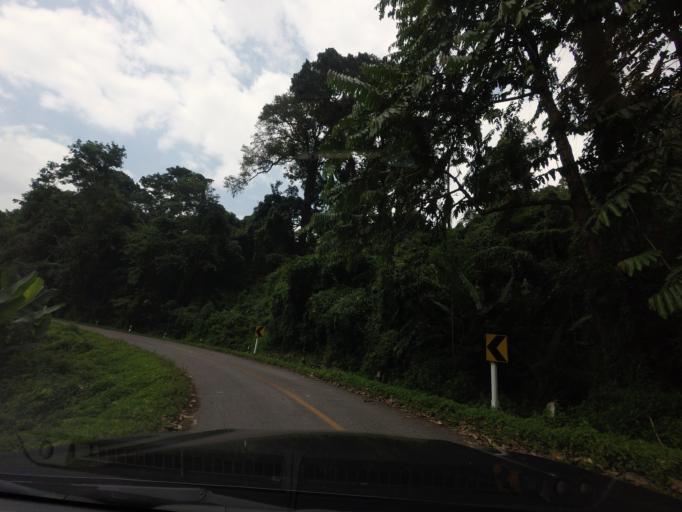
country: TH
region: Uttaradit
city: Nam Pat
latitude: 17.7214
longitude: 100.9484
